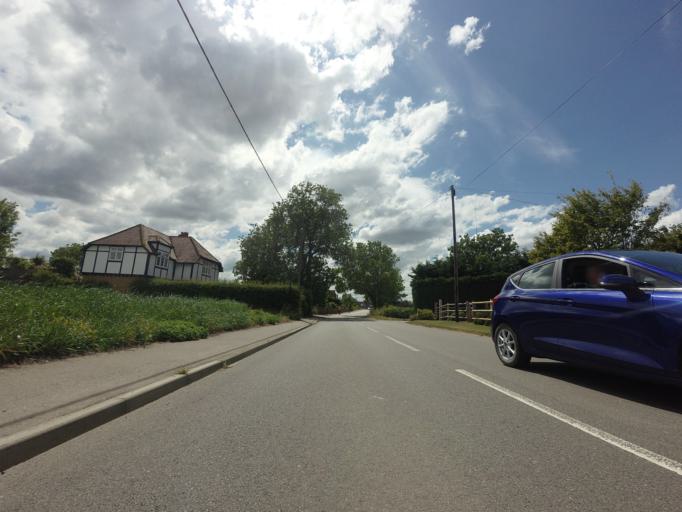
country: GB
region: England
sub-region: Kent
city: Hoo
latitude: 51.4259
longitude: 0.5737
